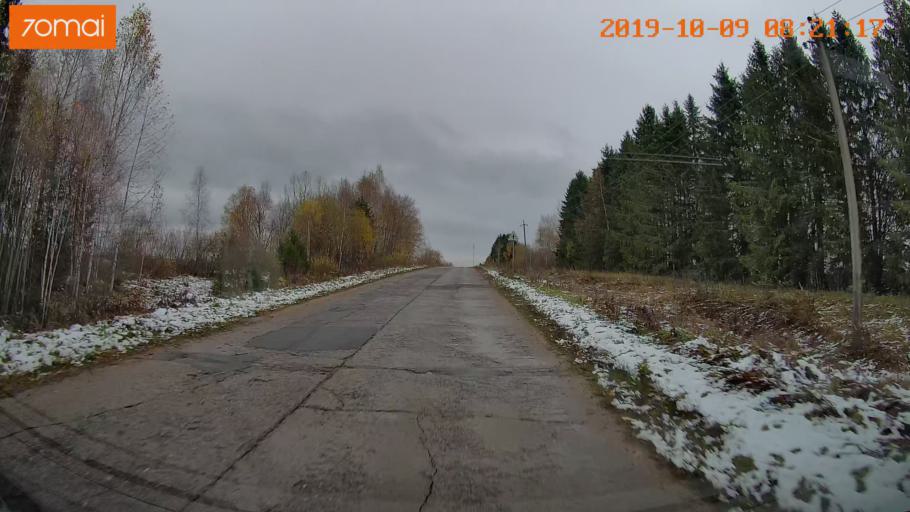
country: RU
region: Vologda
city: Gryazovets
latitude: 58.7422
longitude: 40.2745
